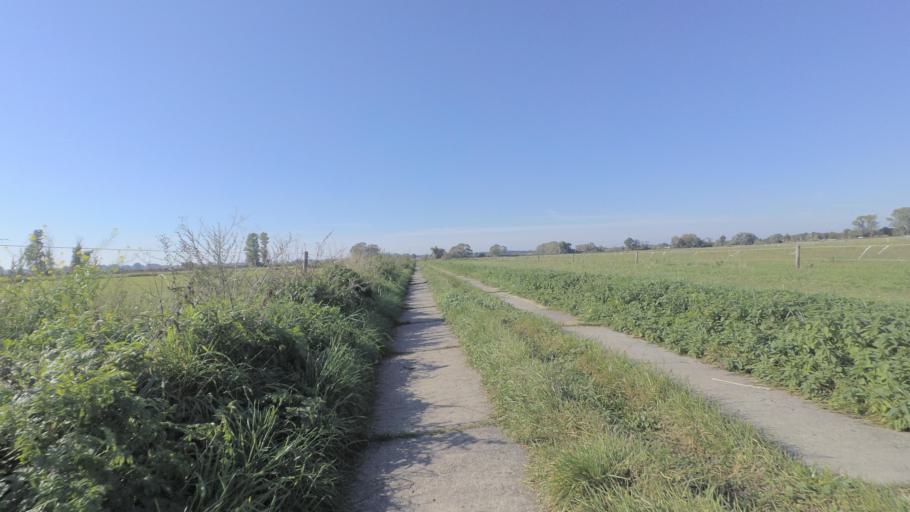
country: DE
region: Brandenburg
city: Rangsdorf
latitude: 52.3030
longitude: 13.3640
